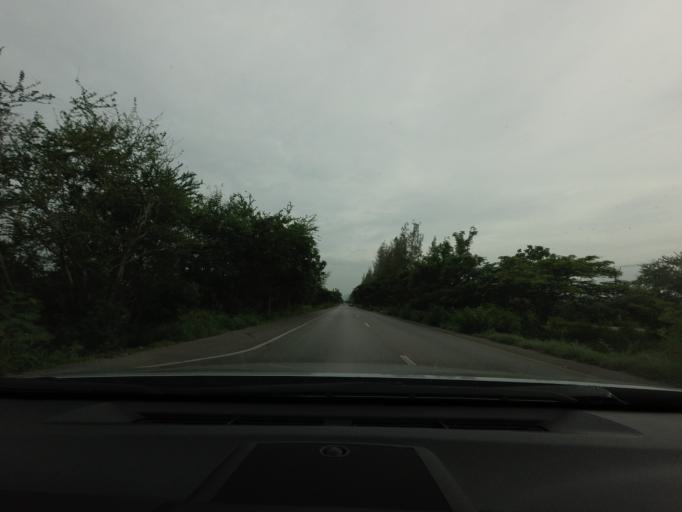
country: TH
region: Phetchaburi
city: Cha-am
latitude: 12.7410
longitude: 99.9295
